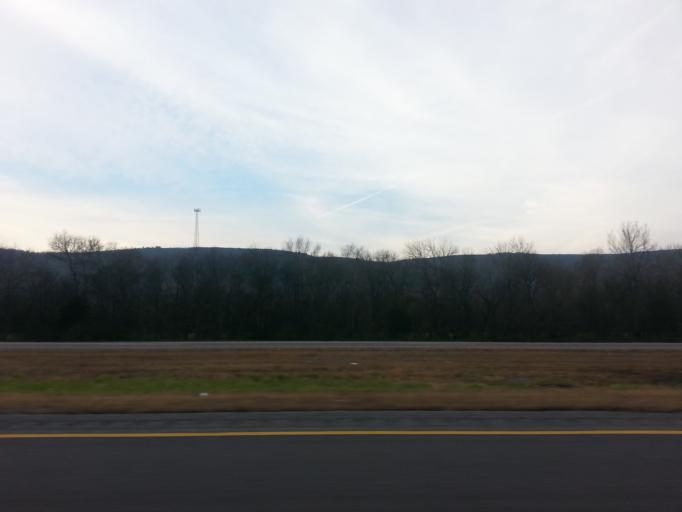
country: US
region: Tennessee
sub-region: Rhea County
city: Spring City
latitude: 35.6075
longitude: -84.9172
